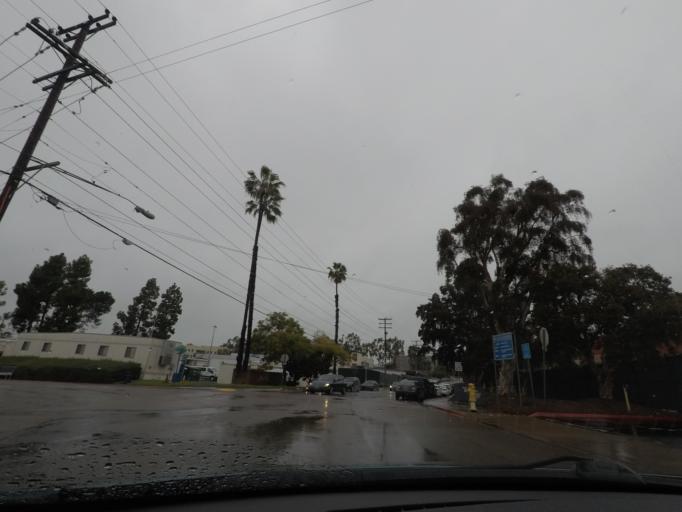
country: US
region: California
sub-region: San Diego County
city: San Diego
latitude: 32.7948
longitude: -117.1544
